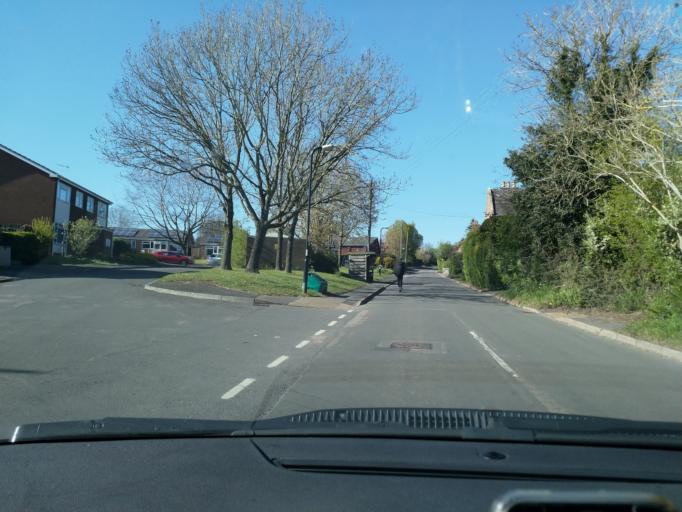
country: GB
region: England
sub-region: Warwickshire
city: Warwick
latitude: 52.2734
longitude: -1.6308
